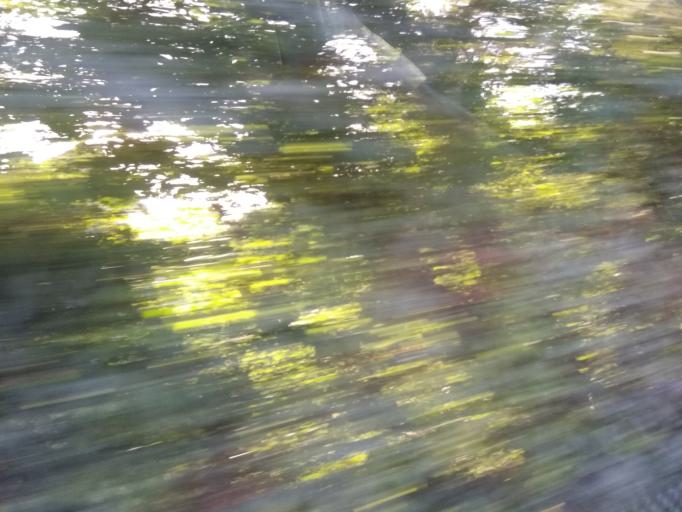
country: DE
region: Baden-Wuerttemberg
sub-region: Karlsruhe Region
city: Mosbach
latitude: 49.3554
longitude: 9.1518
